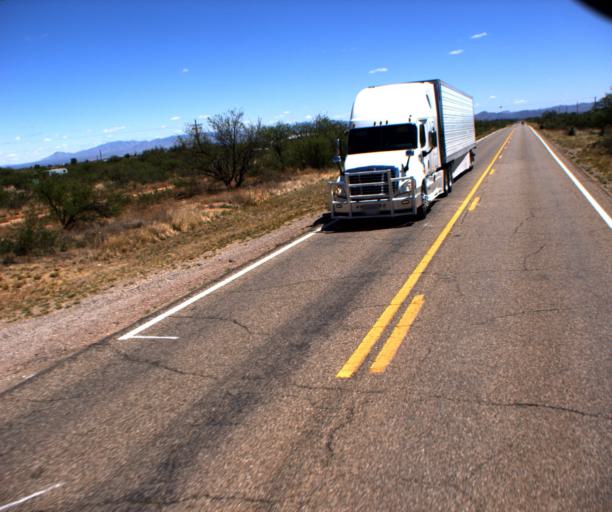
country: US
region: Arizona
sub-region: Cochise County
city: Huachuca City
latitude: 31.6921
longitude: -110.3789
